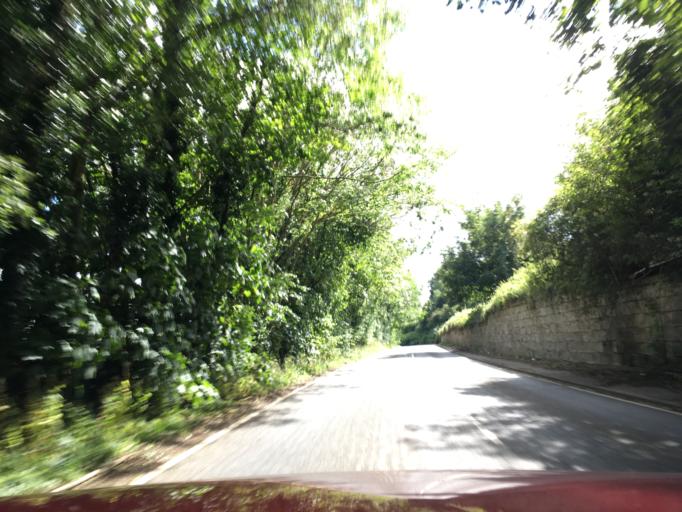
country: GB
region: England
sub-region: Leicestershire
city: Coalville
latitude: 52.7522
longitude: -1.4165
